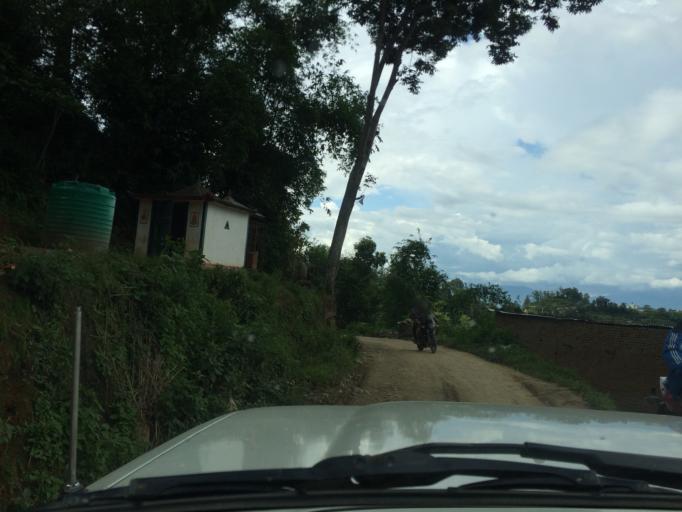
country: NP
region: Central Region
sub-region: Bagmati Zone
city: Patan
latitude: 27.5875
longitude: 85.3087
